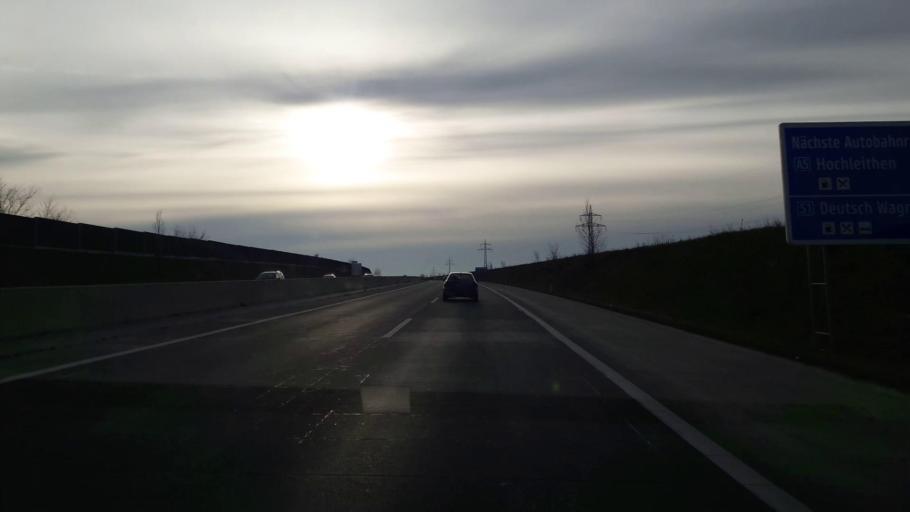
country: AT
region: Lower Austria
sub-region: Politischer Bezirk Mistelbach
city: Gaweinstal
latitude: 48.5127
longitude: 16.6114
